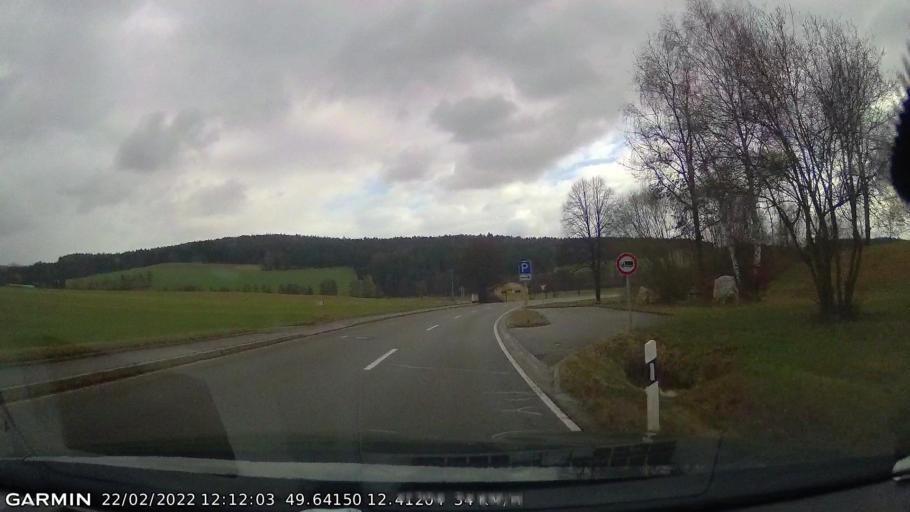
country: DE
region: Bavaria
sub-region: Upper Palatinate
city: Pleystein
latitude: 49.6416
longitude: 12.4120
